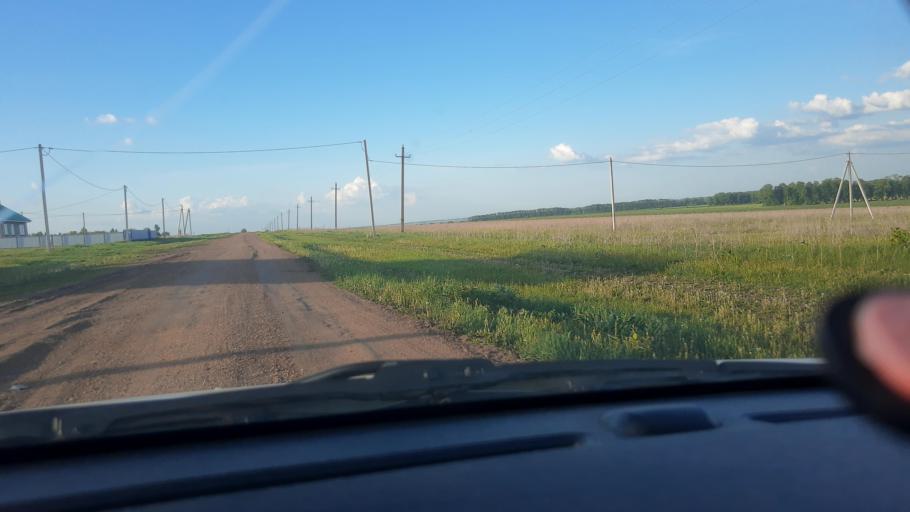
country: RU
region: Bashkortostan
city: Karmaskaly
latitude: 54.3845
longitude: 55.9410
